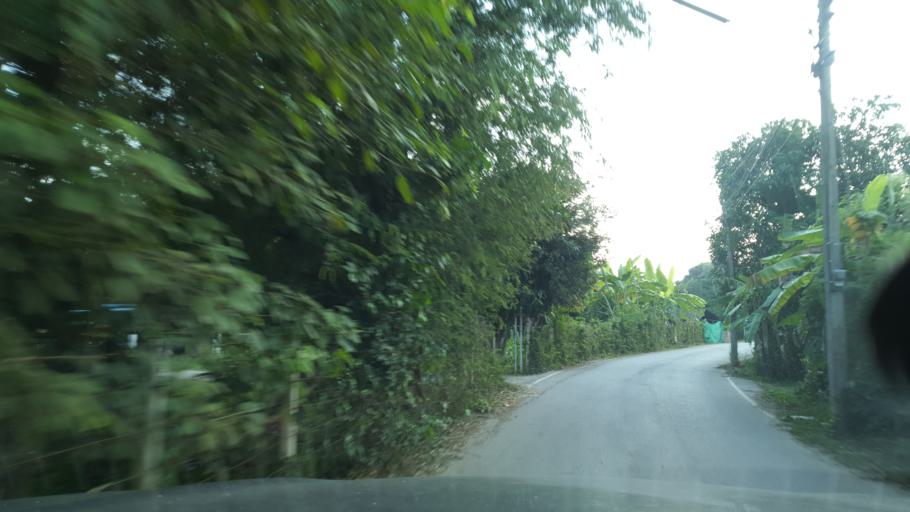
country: TH
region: Chiang Mai
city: San Sai
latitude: 18.8665
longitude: 99.0763
